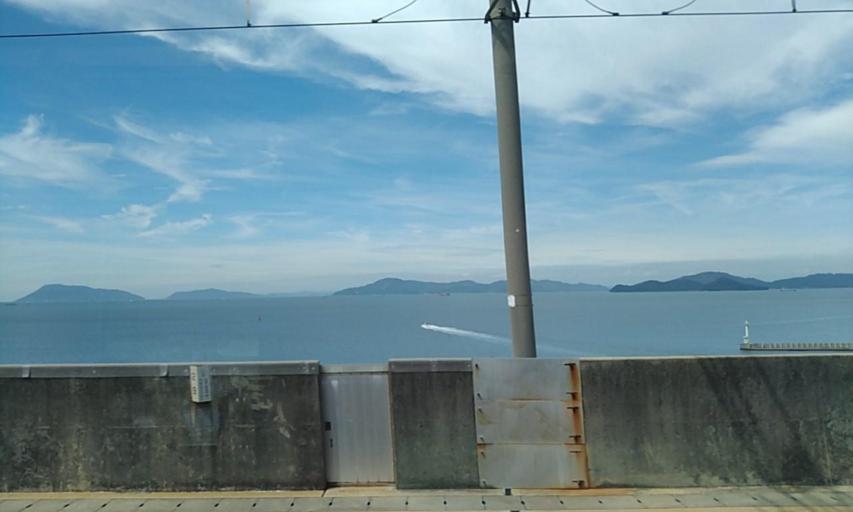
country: JP
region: Kagawa
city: Sakaidecho
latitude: 34.3227
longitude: 133.8241
